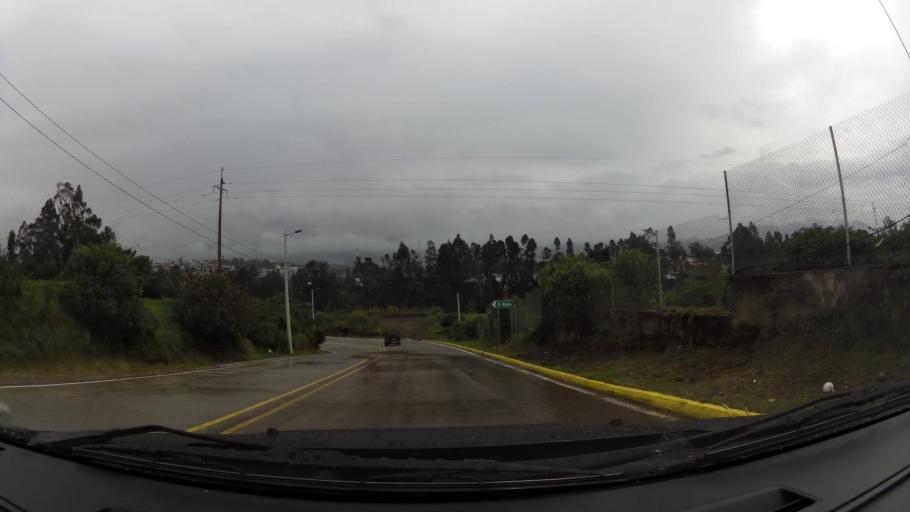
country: EC
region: Pichincha
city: Sangolqui
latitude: -0.2862
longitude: -78.4581
